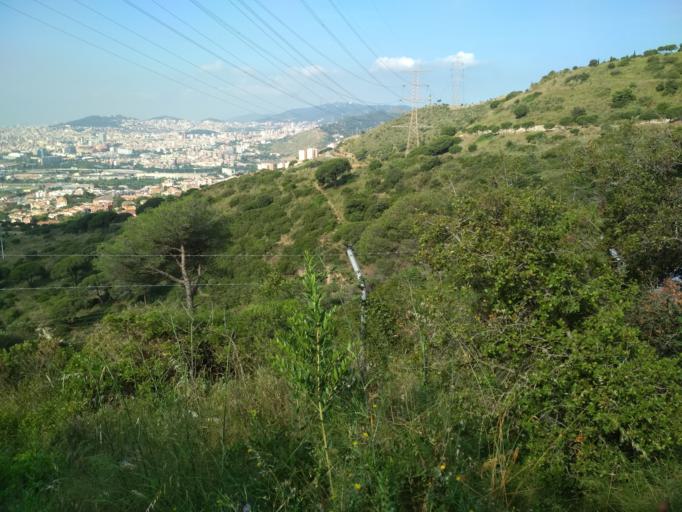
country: ES
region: Catalonia
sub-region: Provincia de Barcelona
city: Santa Coloma de Gramenet
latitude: 41.4696
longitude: 2.2123
